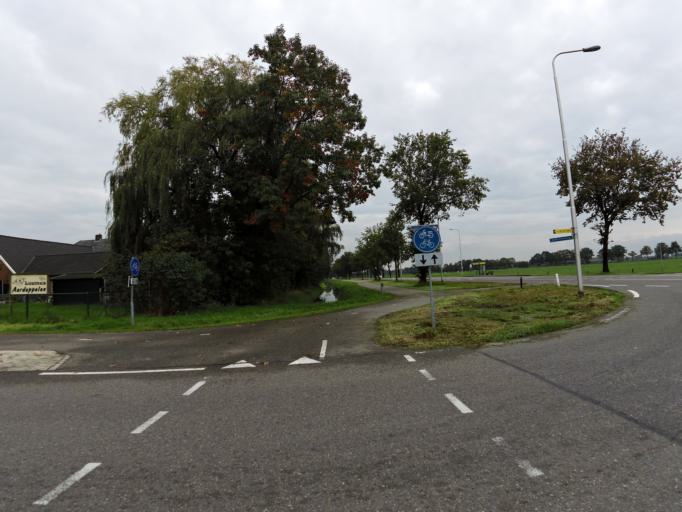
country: NL
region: Gelderland
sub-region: Oude IJsselstreek
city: Gendringen
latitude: 51.8979
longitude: 6.3576
